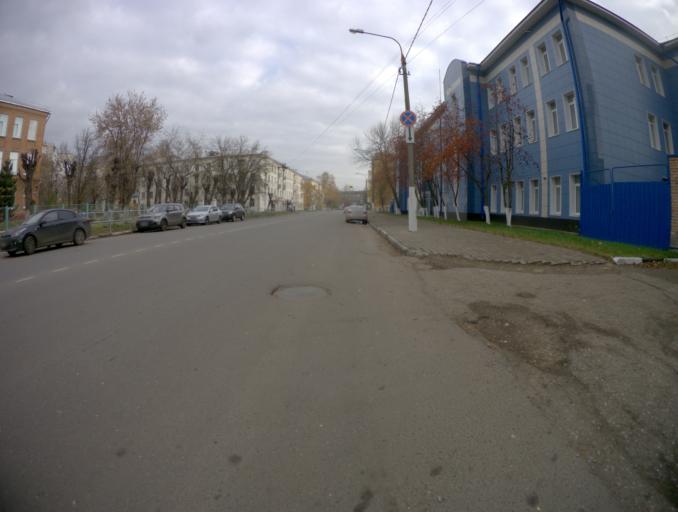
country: RU
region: Moskovskaya
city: Orekhovo-Zuyevo
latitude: 55.8041
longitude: 38.9662
